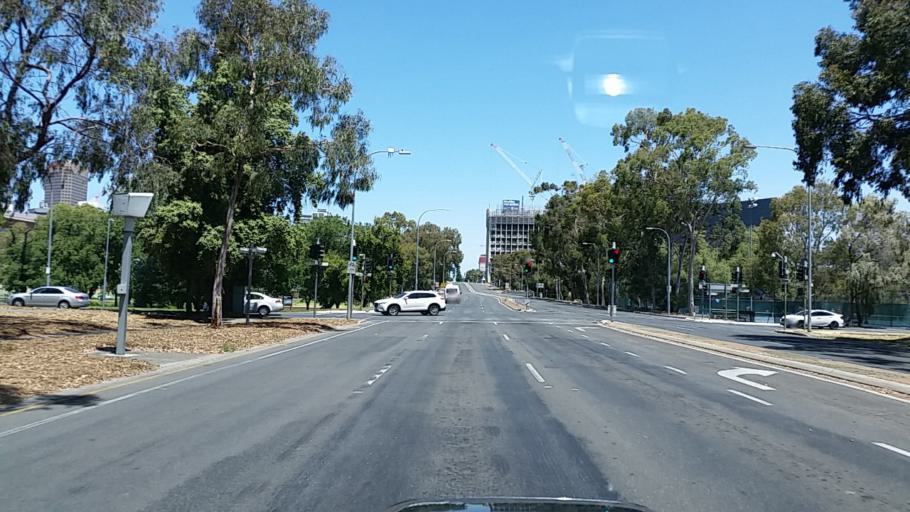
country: AU
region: South Australia
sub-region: Adelaide
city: North Adelaide
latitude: -34.9171
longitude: 138.5931
